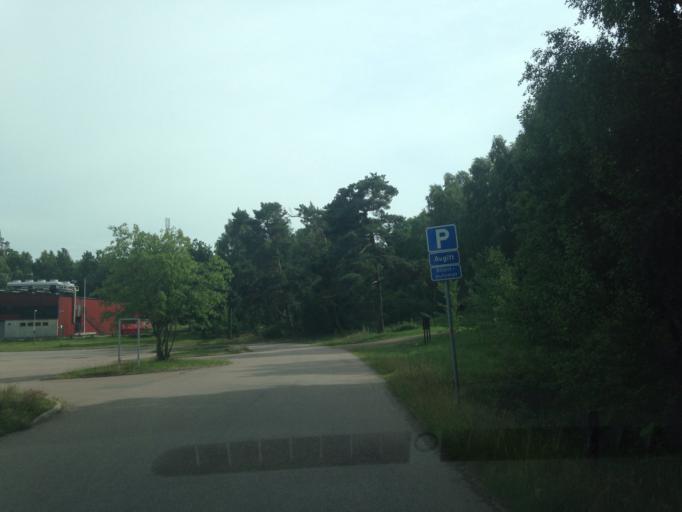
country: SE
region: Vaestra Goetaland
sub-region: Goteborg
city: Majorna
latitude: 57.7503
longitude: 11.9132
